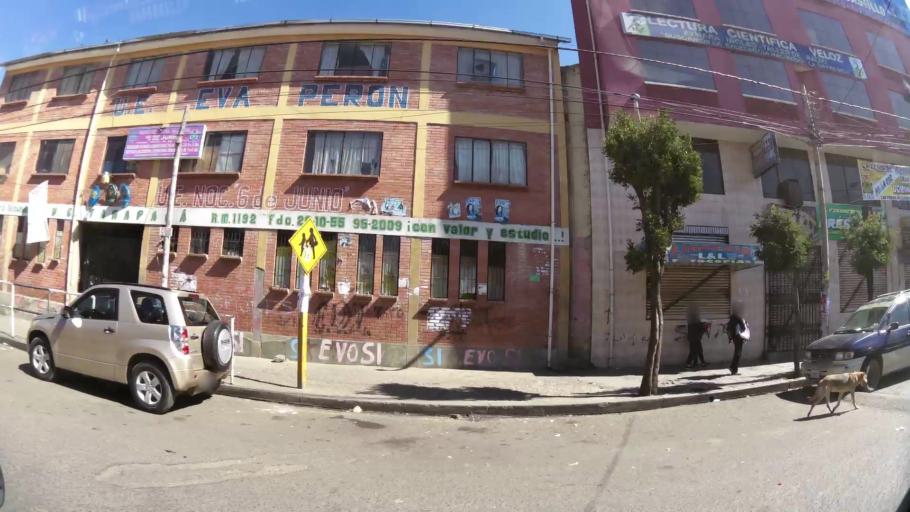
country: BO
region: La Paz
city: La Paz
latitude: -16.5096
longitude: -68.1595
